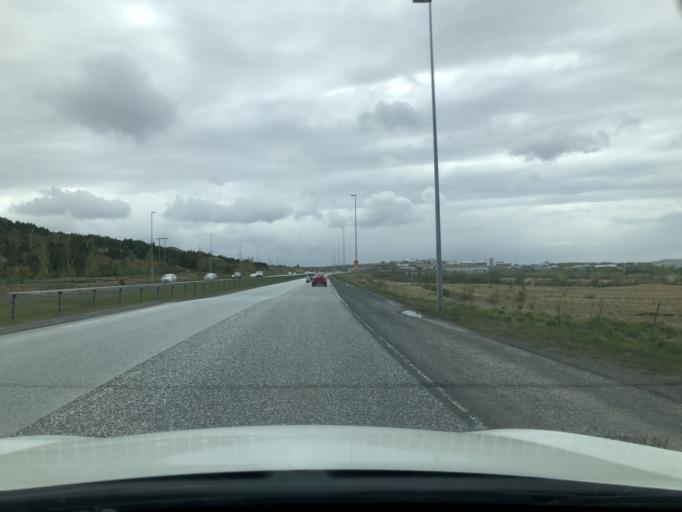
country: IS
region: Capital Region
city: Mosfellsbaer
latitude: 64.1529
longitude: -21.7386
